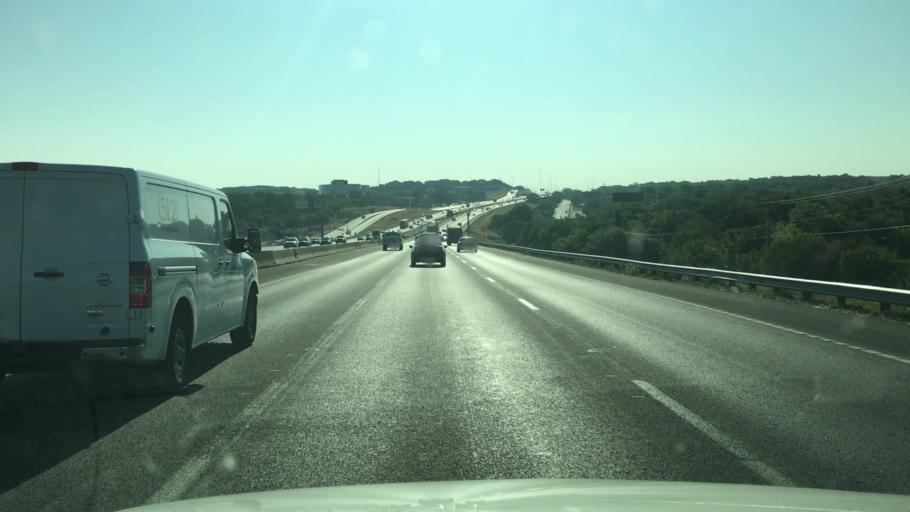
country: US
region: Texas
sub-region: Tarrant County
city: Haltom City
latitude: 32.7600
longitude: -97.2442
